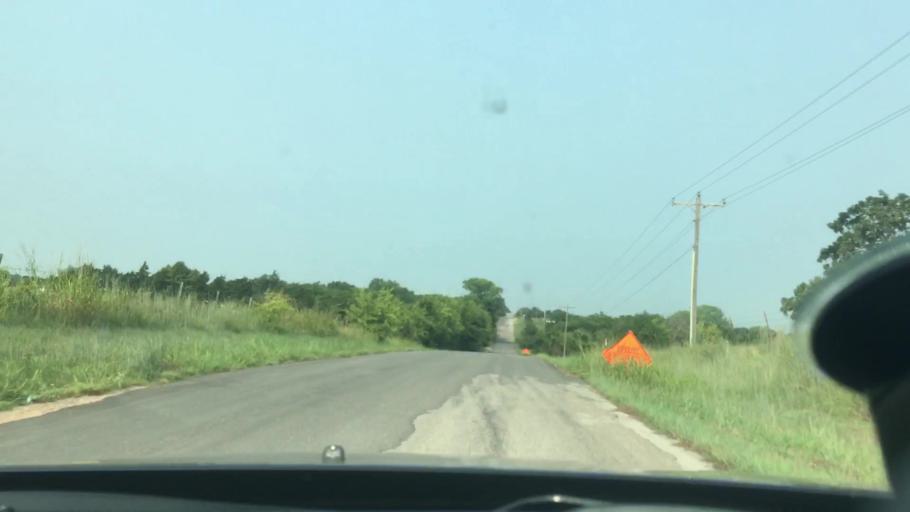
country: US
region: Oklahoma
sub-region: Garvin County
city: Lindsay
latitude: 34.8120
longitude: -97.6401
